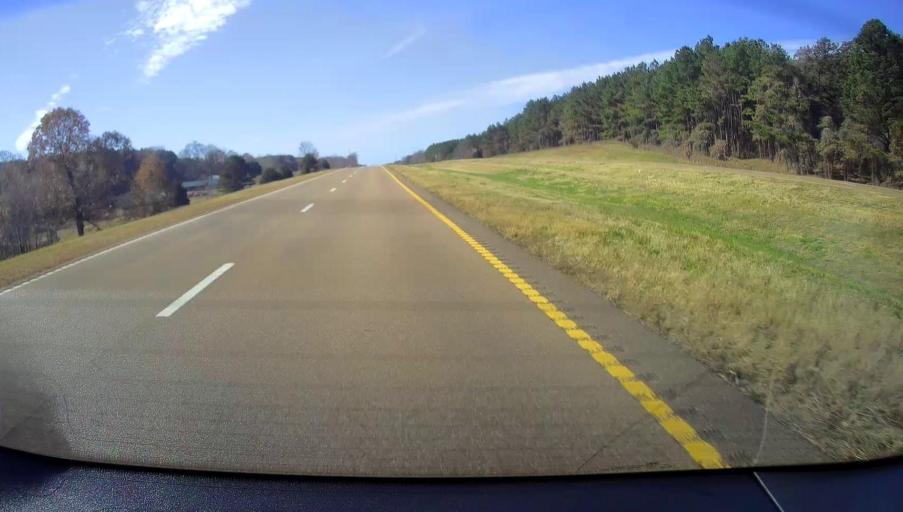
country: US
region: Mississippi
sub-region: Benton County
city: Ashland
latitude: 34.9481
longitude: -89.1095
